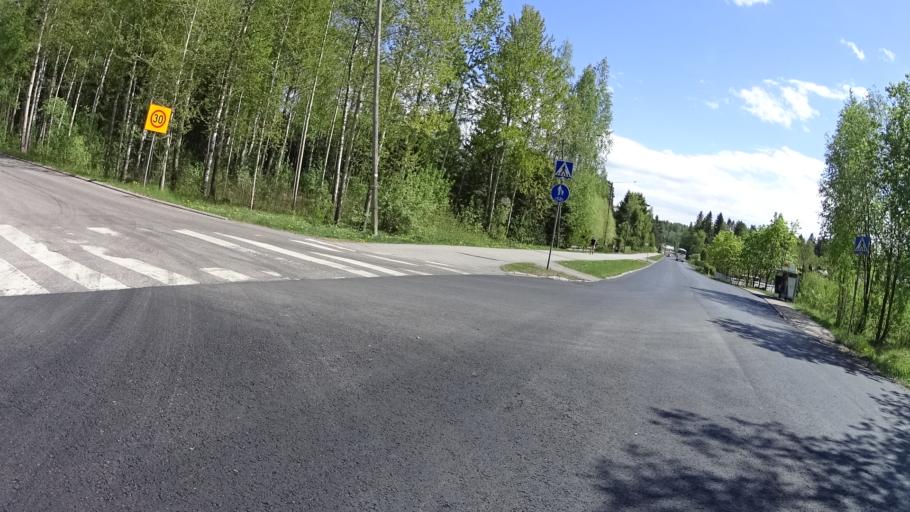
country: FI
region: Uusimaa
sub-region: Helsinki
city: Kilo
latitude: 60.2415
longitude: 24.7640
